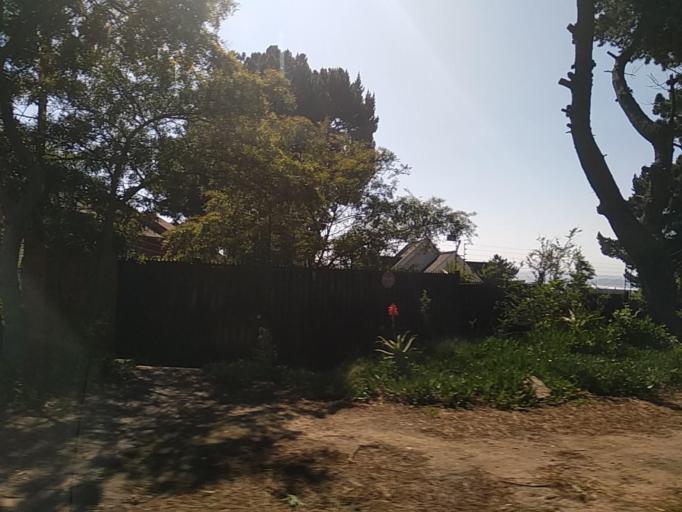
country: CL
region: Valparaiso
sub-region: Provincia de Valparaiso
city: Vina del Mar
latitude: -32.9390
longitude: -71.5383
